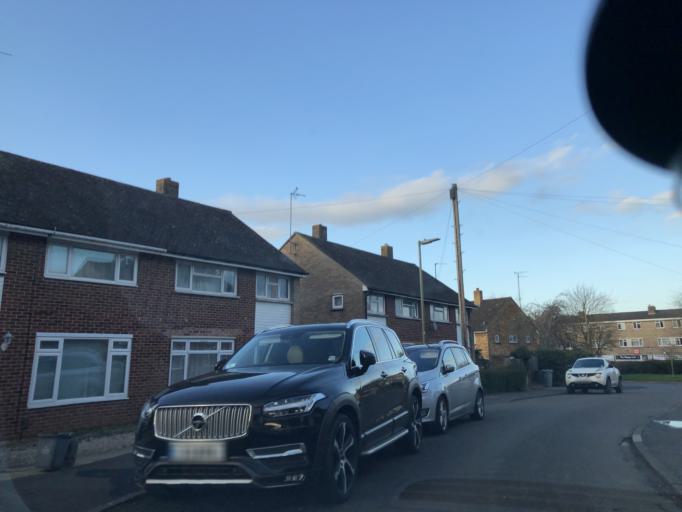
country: GB
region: England
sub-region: Oxfordshire
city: Witney
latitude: 51.7867
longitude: -1.5034
